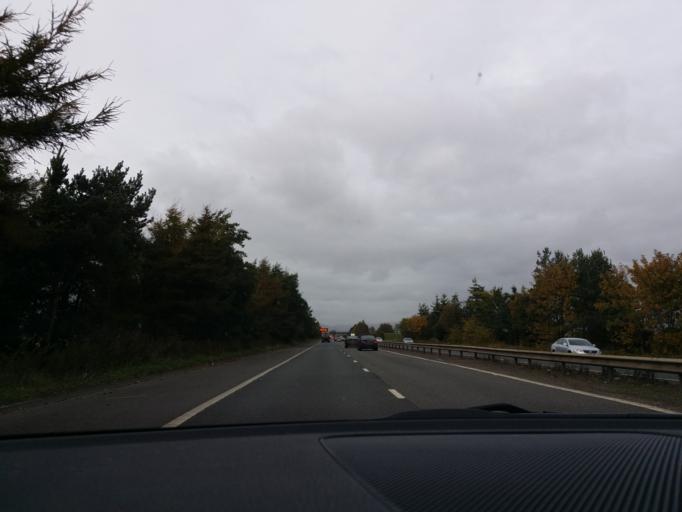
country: GB
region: Scotland
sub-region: Falkirk
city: Falkirk
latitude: 56.0239
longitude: -3.7588
